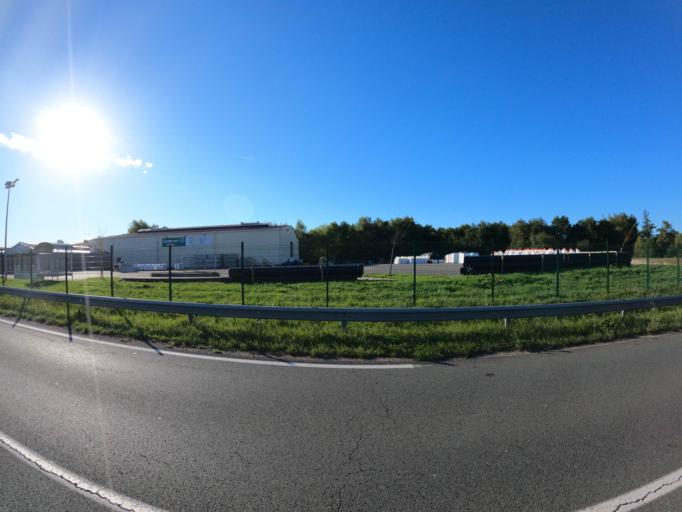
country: FR
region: Bourgogne
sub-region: Departement de Saone-et-Loire
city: Blanzy
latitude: 46.7056
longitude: 4.4119
